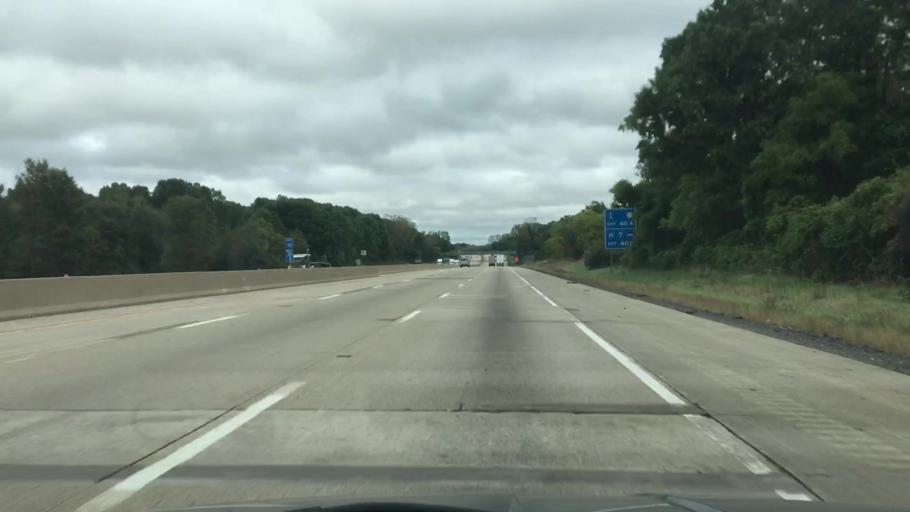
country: US
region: Indiana
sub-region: LaPorte County
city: Trail Creek
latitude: 41.6811
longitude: -86.8232
